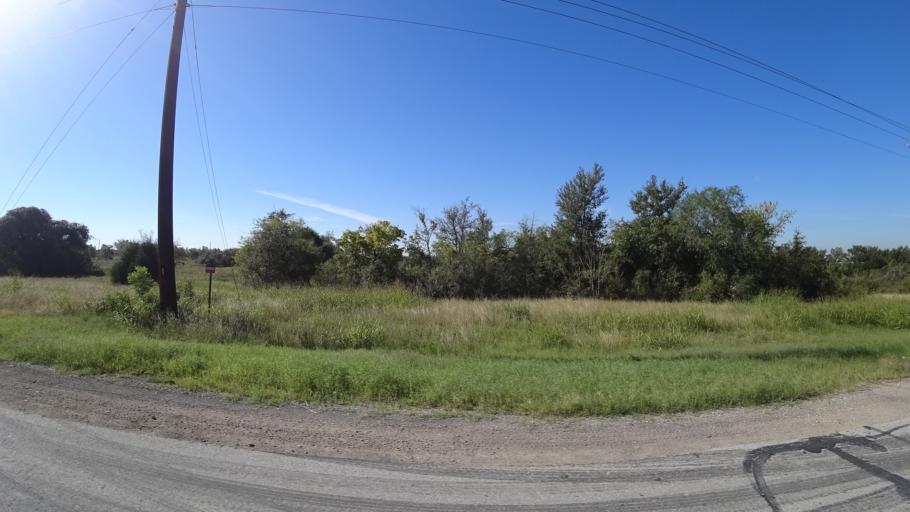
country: US
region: Texas
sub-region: Travis County
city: Hornsby Bend
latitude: 30.2519
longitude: -97.6001
